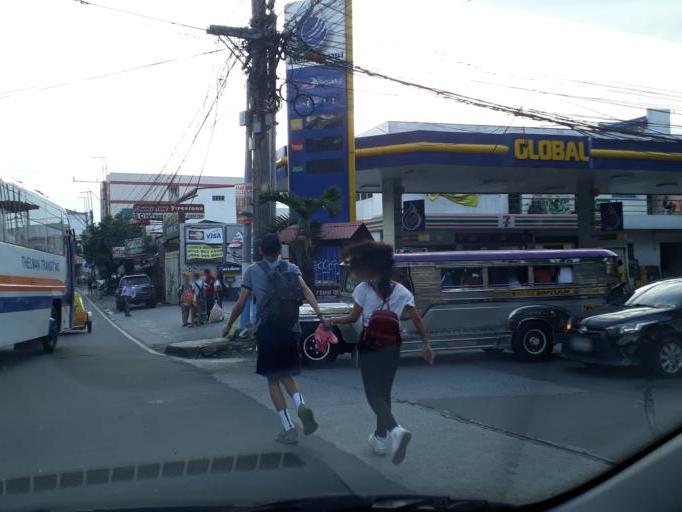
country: PH
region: Calabarzon
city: Bagong Pagasa
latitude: 14.6637
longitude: 121.0225
